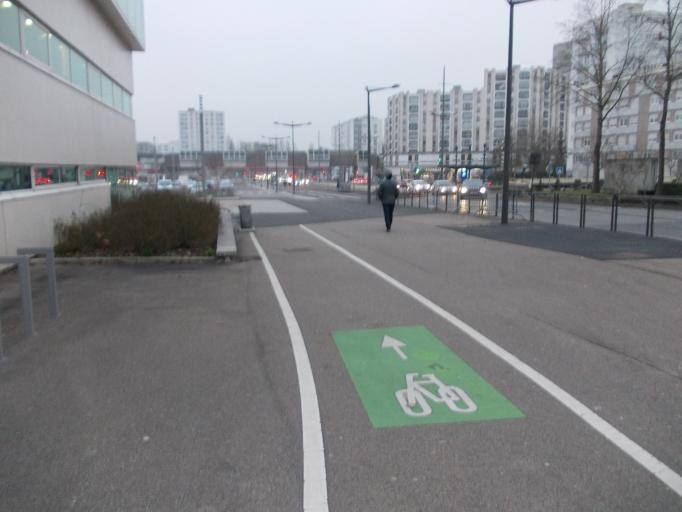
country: FR
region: Lorraine
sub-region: Departement de Meurthe-et-Moselle
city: Vandoeuvre-les-Nancy
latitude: 48.6629
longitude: 6.1727
